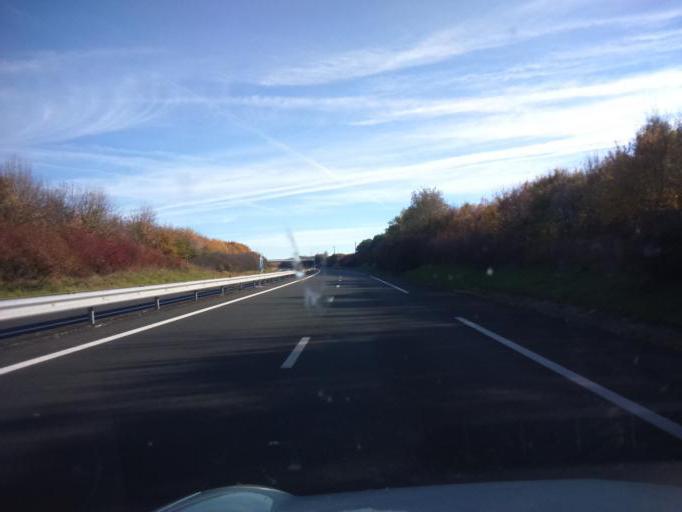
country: FR
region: Poitou-Charentes
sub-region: Departement de la Charente-Maritime
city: Tonnay-Charente
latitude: 45.9546
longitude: -0.8936
